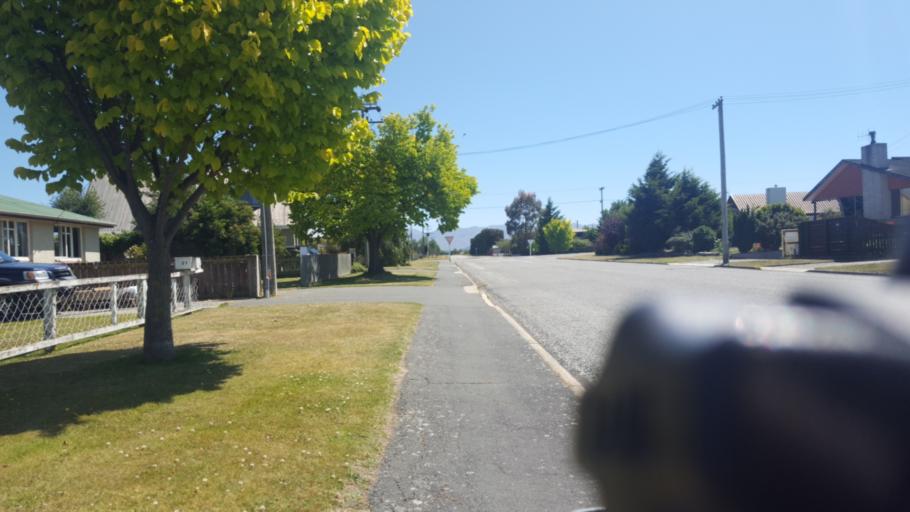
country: NZ
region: Otago
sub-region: Dunedin City
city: Dunedin
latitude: -45.1265
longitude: 170.1060
